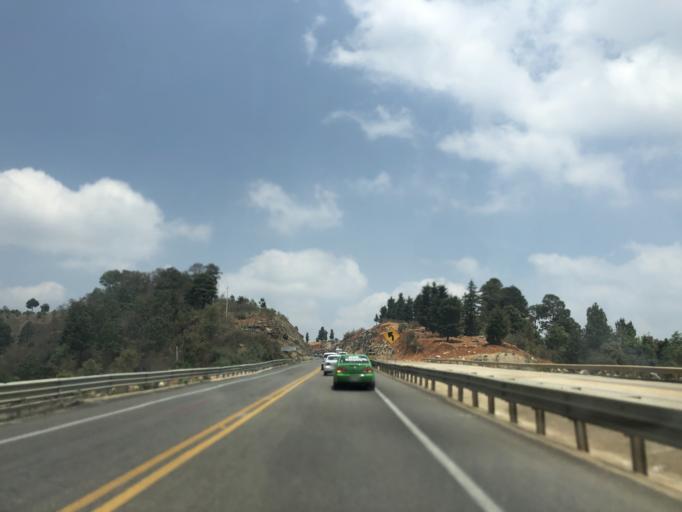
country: MX
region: Chiapas
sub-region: Zinacantan
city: Nachig
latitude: 16.6886
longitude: -92.7245
